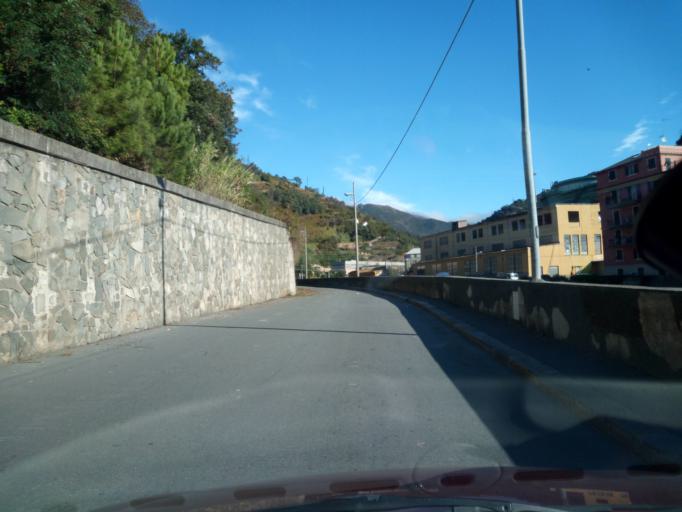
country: IT
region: Liguria
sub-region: Provincia di Genova
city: Mele
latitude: 44.4321
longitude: 8.8195
